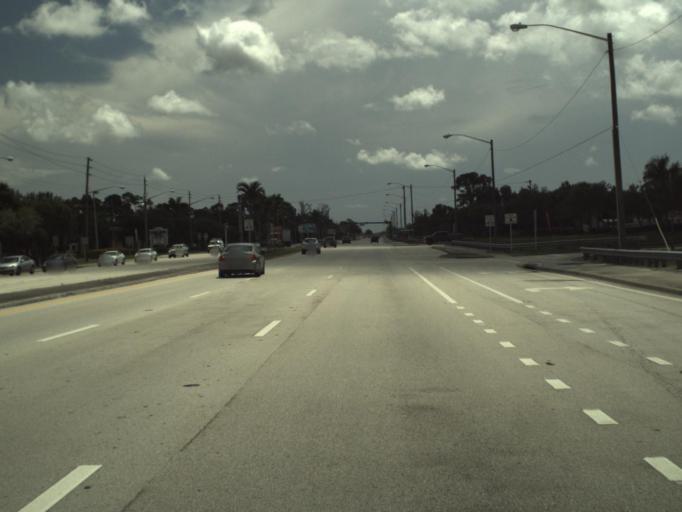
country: US
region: Florida
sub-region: Palm Beach County
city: Wellington
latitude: 26.6171
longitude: -80.2043
